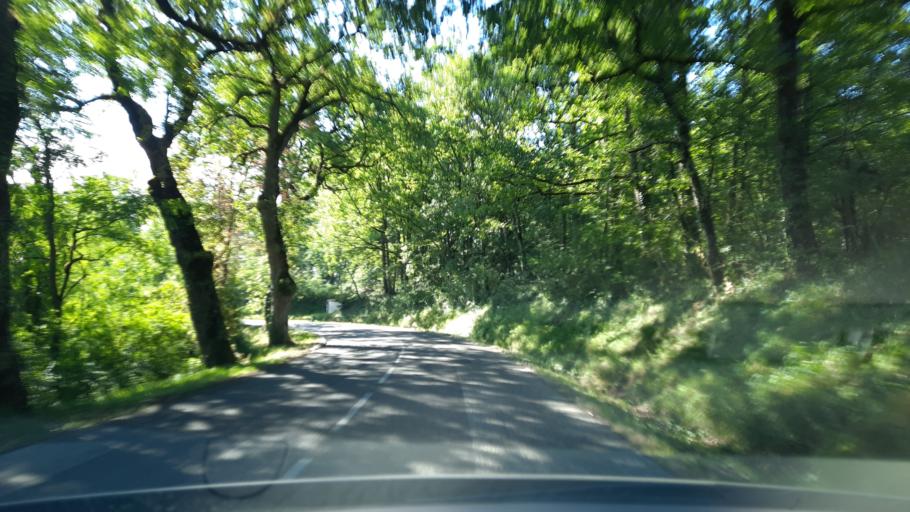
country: FR
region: Midi-Pyrenees
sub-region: Departement du Tarn-et-Garonne
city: Molieres
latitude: 44.1855
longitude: 1.3463
